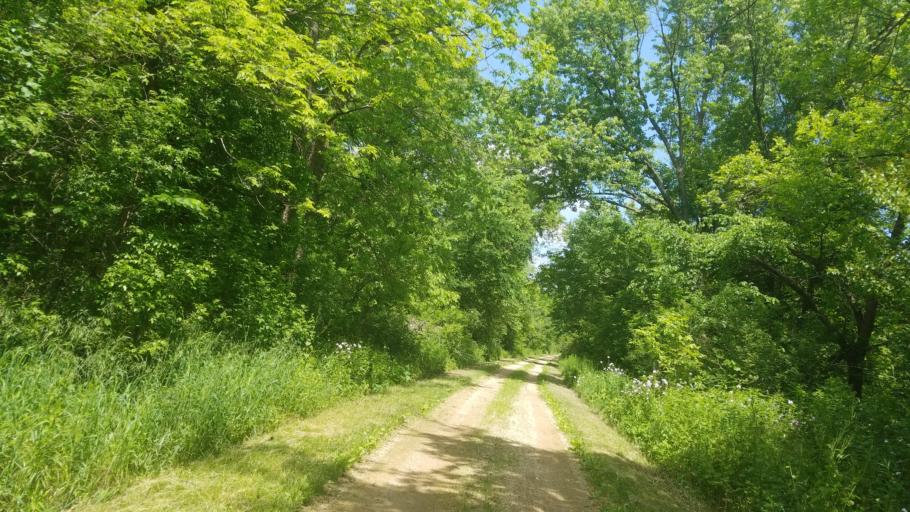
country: US
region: Wisconsin
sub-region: Dunn County
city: Menomonie
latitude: 44.7842
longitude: -91.9430
